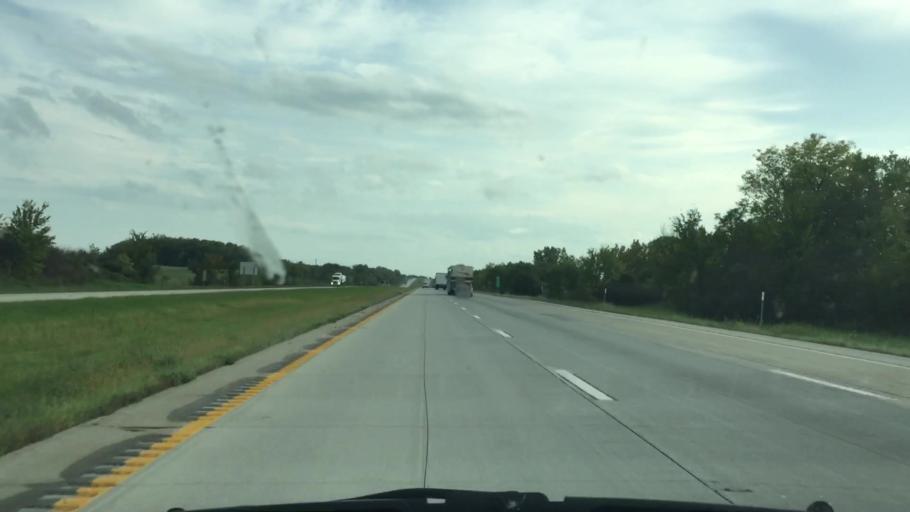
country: US
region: Missouri
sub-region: Daviess County
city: Gallatin
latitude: 39.9931
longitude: -94.0956
